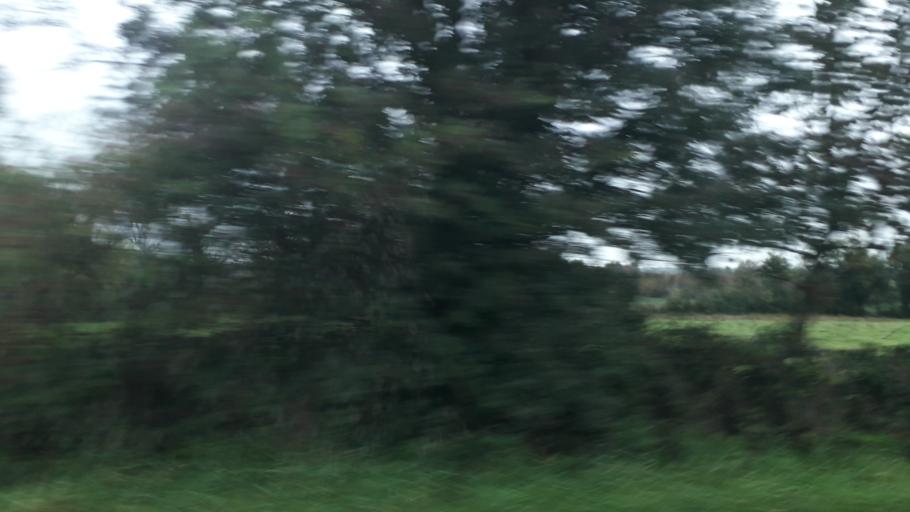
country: IE
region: Leinster
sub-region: An Longfort
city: Edgeworthstown
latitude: 53.6743
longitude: -7.5554
